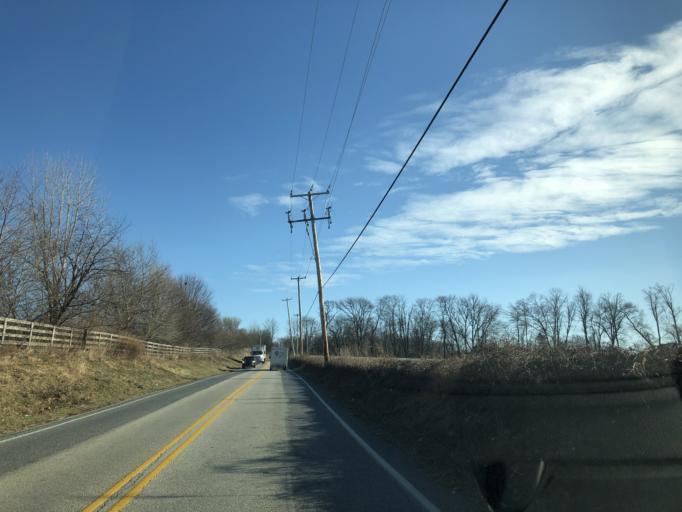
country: US
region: Pennsylvania
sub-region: Chester County
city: Toughkenamon
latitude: 39.8525
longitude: -75.7701
